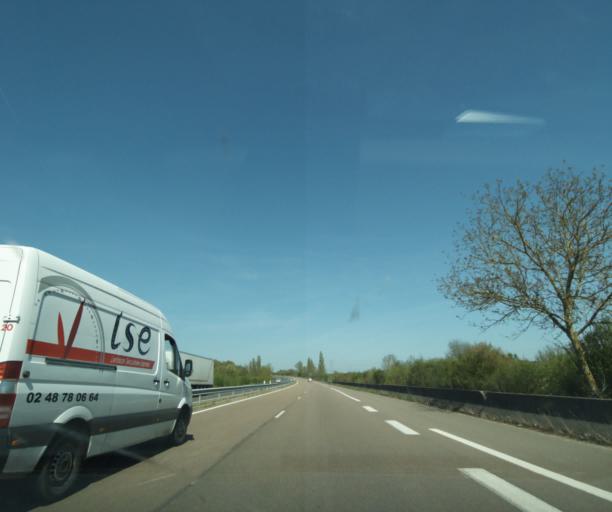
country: FR
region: Bourgogne
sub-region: Departement de la Nievre
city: La Charite-sur-Loire
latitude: 47.1603
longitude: 3.0507
